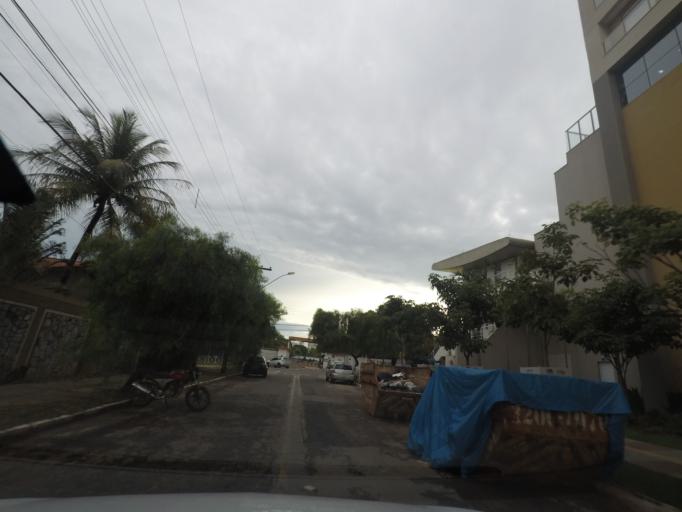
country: BR
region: Goias
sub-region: Goiania
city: Goiania
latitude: -16.7039
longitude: -49.2557
